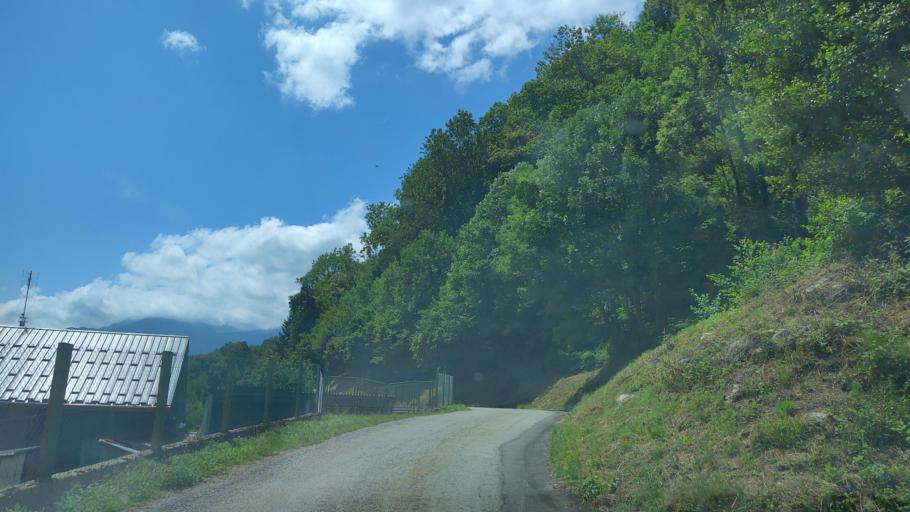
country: FR
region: Rhone-Alpes
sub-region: Departement de la Savoie
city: Aiton
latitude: 45.5084
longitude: 6.2885
